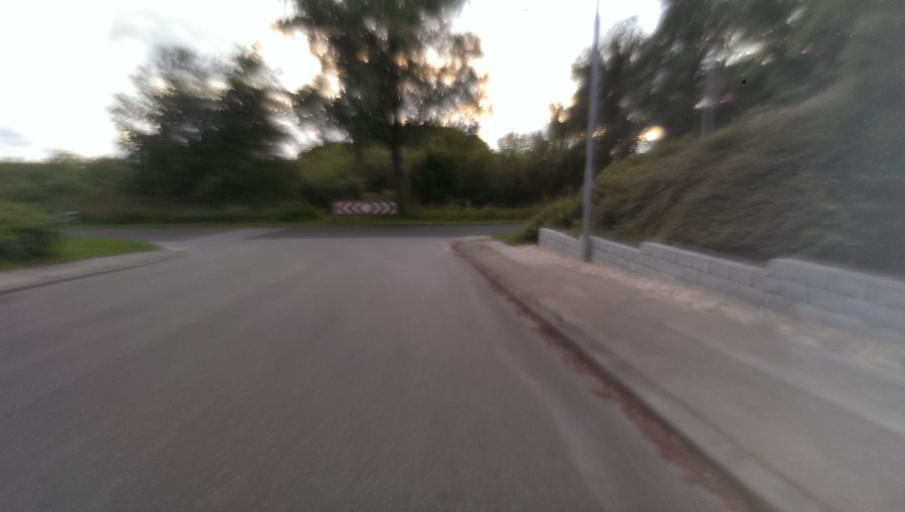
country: DK
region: South Denmark
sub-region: Esbjerg Kommune
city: Tjaereborg
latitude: 55.4721
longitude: 8.5690
